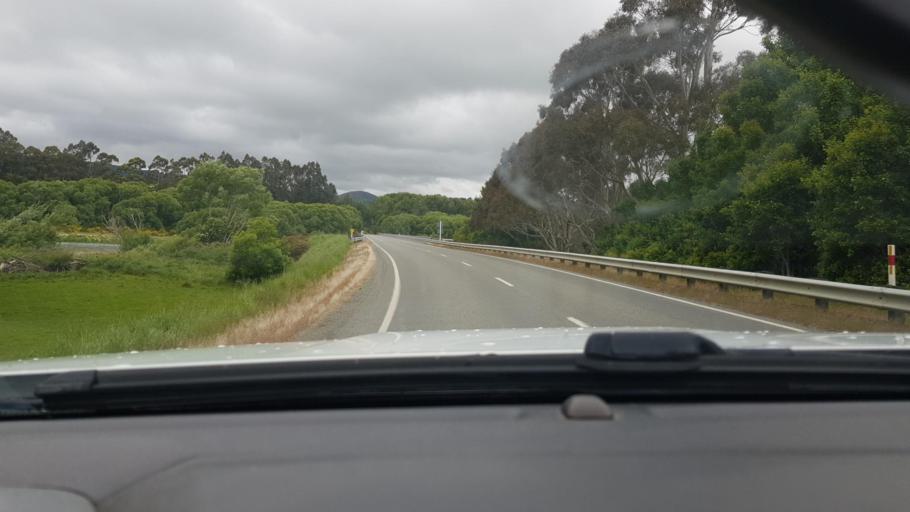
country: NZ
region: Southland
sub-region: Southland District
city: Winton
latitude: -45.8943
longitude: 168.3594
